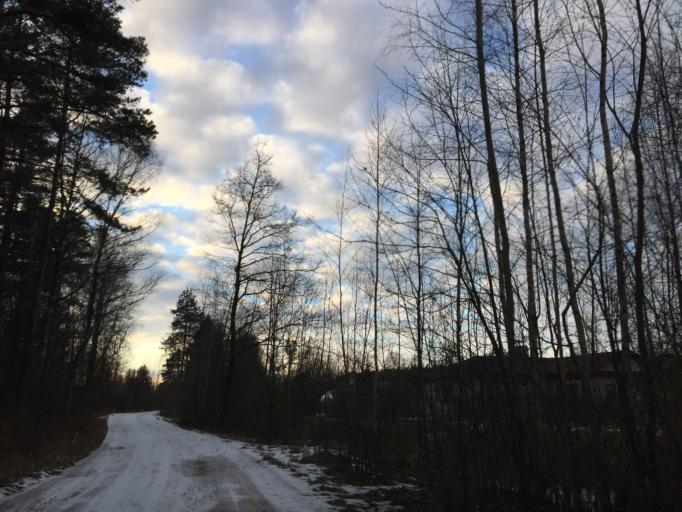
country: LV
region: Babite
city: Pinki
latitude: 56.9189
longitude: 23.8663
